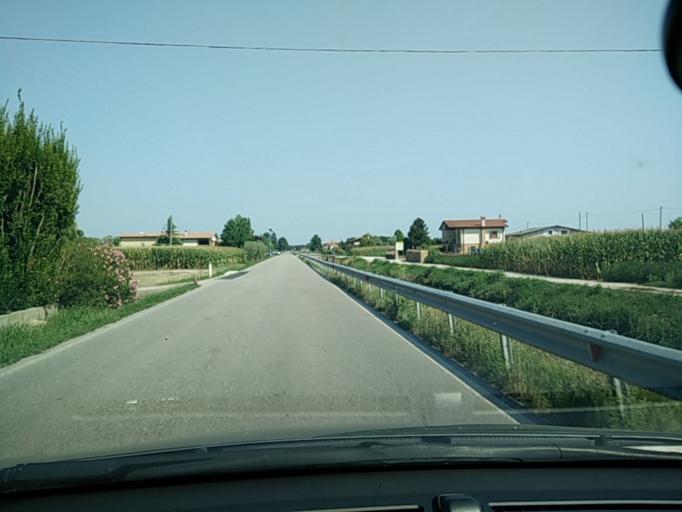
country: IT
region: Veneto
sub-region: Provincia di Venezia
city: Passarella
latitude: 45.6198
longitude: 12.6279
